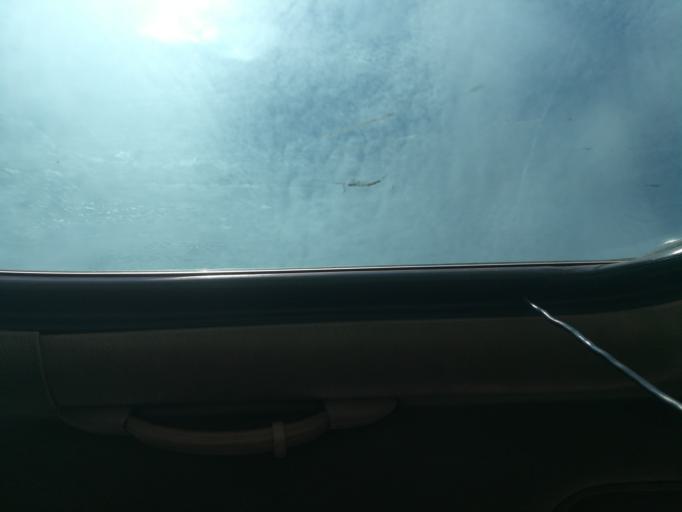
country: NG
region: Lagos
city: Lagos
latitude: 6.4067
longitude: 3.4116
